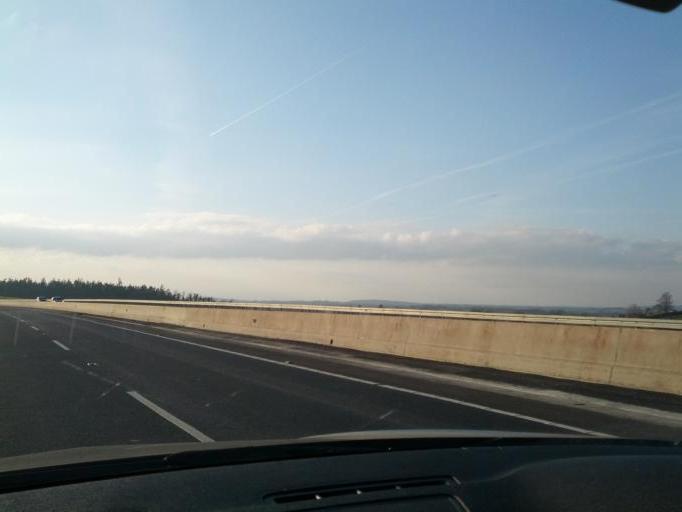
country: IE
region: Munster
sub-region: North Tipperary
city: Templemore
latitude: 52.8870
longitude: -7.9270
